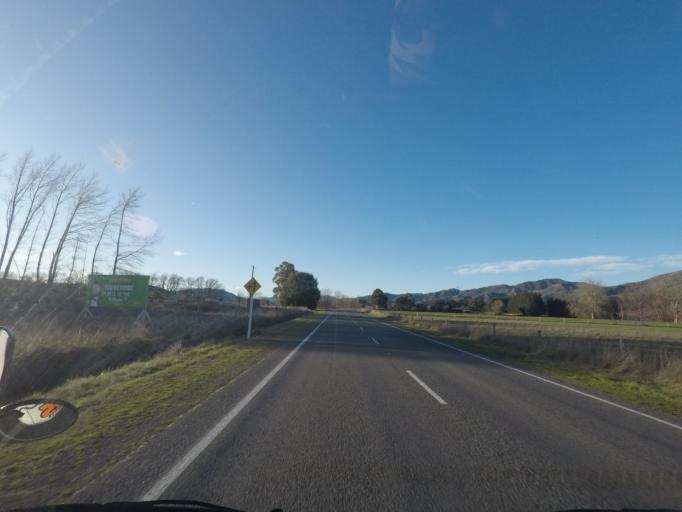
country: NZ
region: Canterbury
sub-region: Kaikoura District
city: Kaikoura
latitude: -42.7118
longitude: 173.2916
